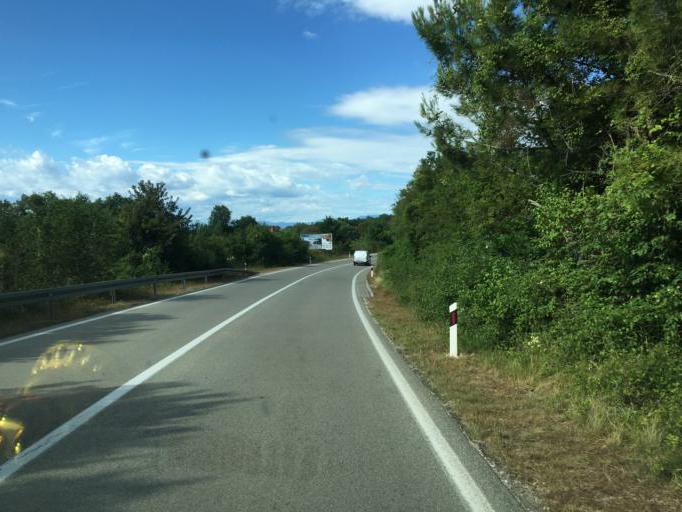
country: HR
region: Primorsko-Goranska
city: Njivice
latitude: 45.0991
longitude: 14.5371
